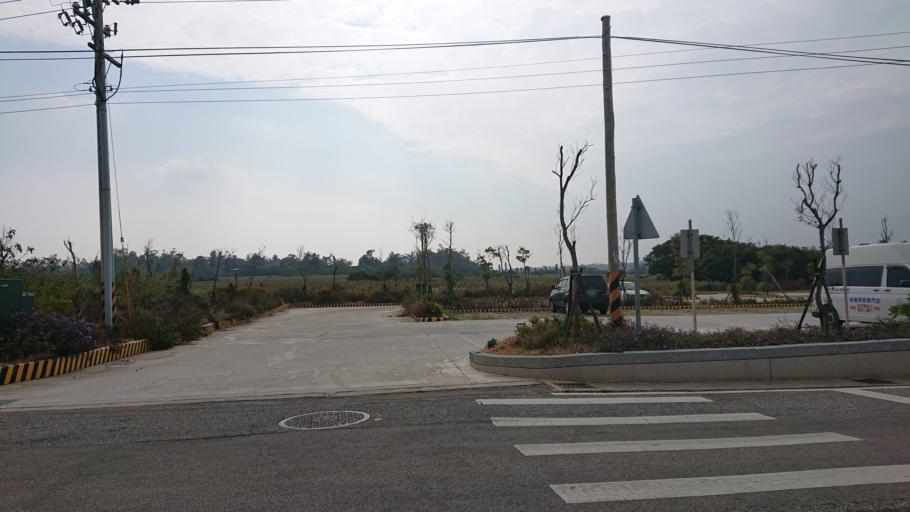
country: TW
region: Fukien
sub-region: Kinmen
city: Jincheng
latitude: 24.4520
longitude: 118.3810
